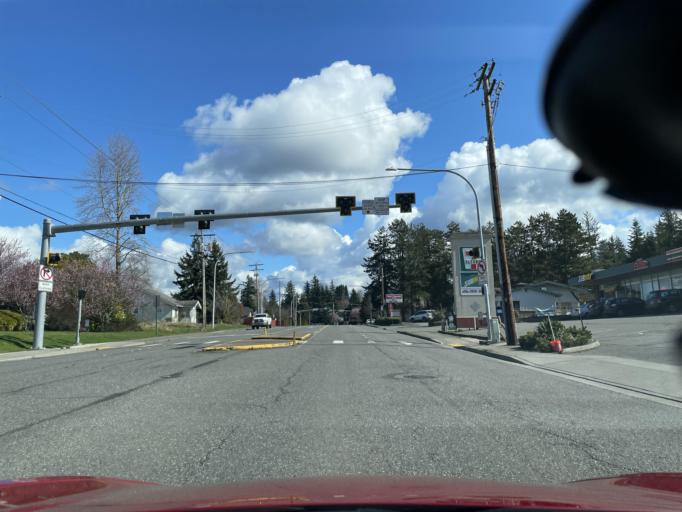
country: US
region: Washington
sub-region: Whatcom County
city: Bellingham
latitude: 48.7449
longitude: -122.4587
